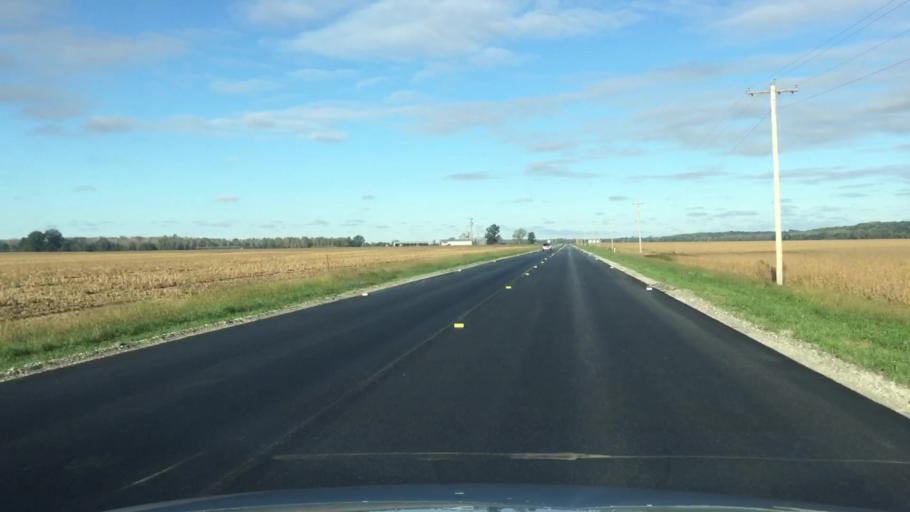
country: US
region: Missouri
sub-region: Howard County
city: New Franklin
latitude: 38.9946
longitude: -92.6569
